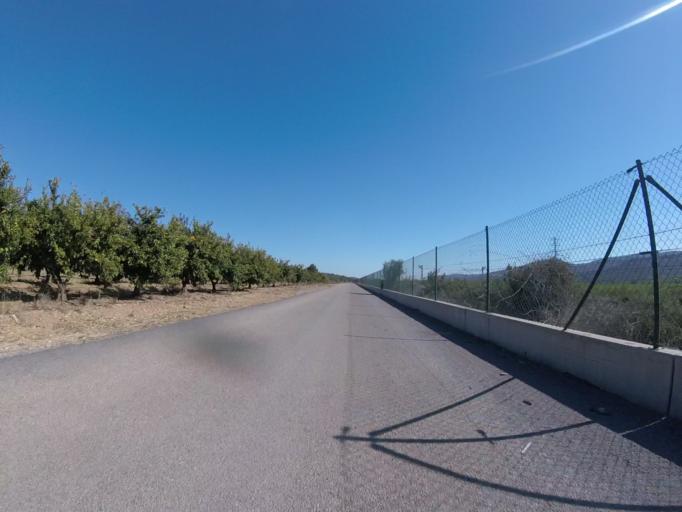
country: ES
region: Valencia
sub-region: Provincia de Castello
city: Alcala de Xivert
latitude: 40.3326
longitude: 0.2504
